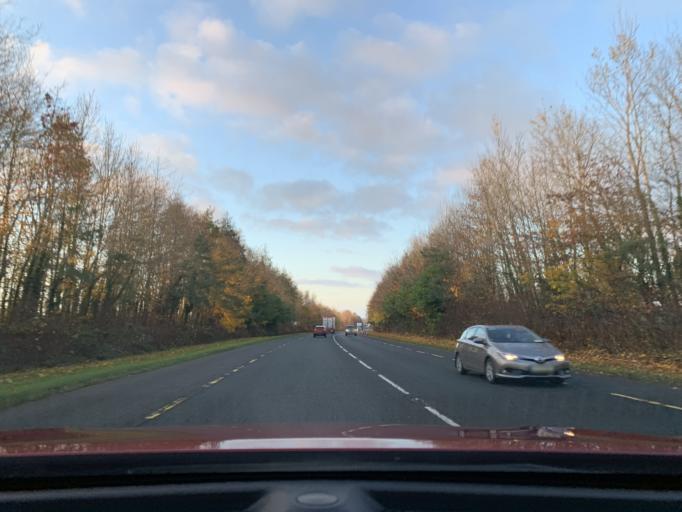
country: IE
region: Leinster
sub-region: An Longfort
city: Longford
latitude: 53.7264
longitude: -7.7687
